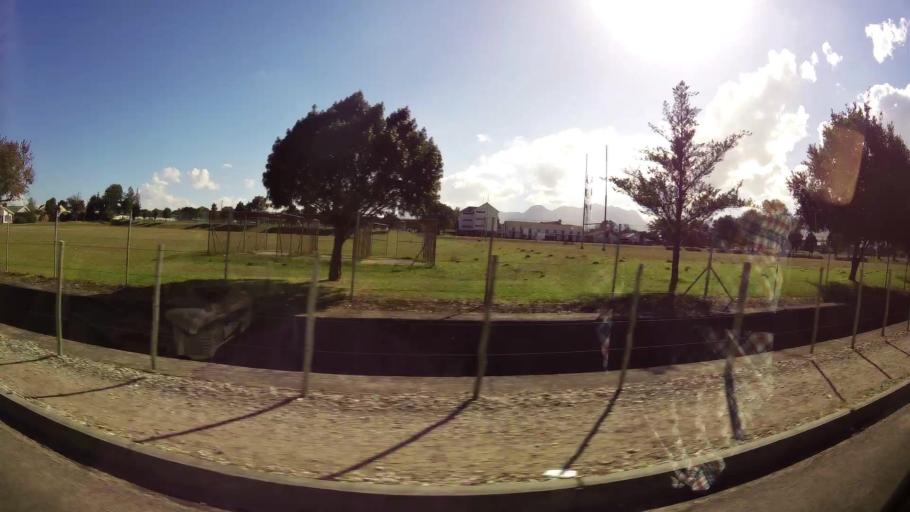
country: ZA
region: Western Cape
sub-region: Eden District Municipality
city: George
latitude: -33.9768
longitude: 22.4469
